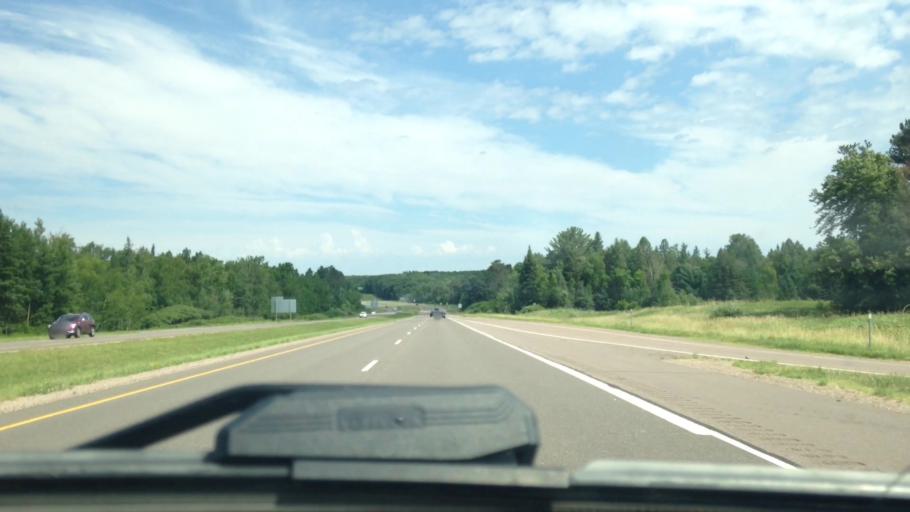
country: US
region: Wisconsin
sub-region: Washburn County
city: Spooner
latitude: 45.8198
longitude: -91.8560
